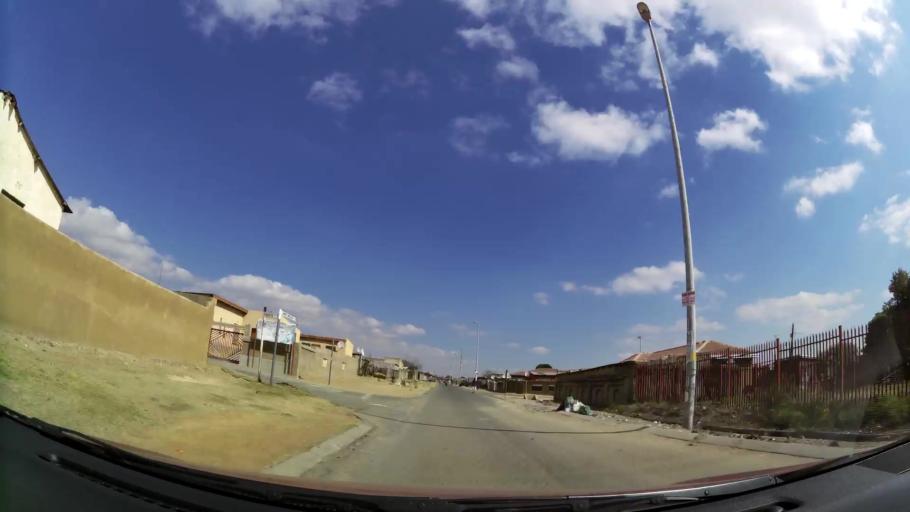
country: ZA
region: Gauteng
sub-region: Ekurhuleni Metropolitan Municipality
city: Tembisa
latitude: -26.0179
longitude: 28.1925
